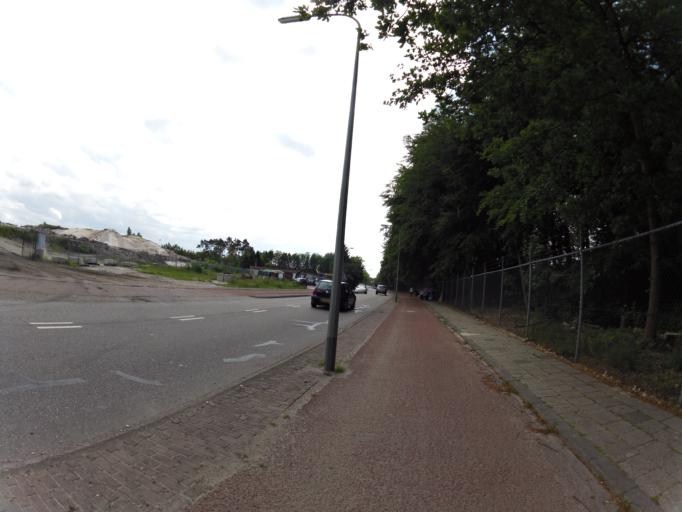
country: NL
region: Limburg
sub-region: Gemeente Brunssum
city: Brunssum
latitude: 50.9380
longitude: 5.9863
